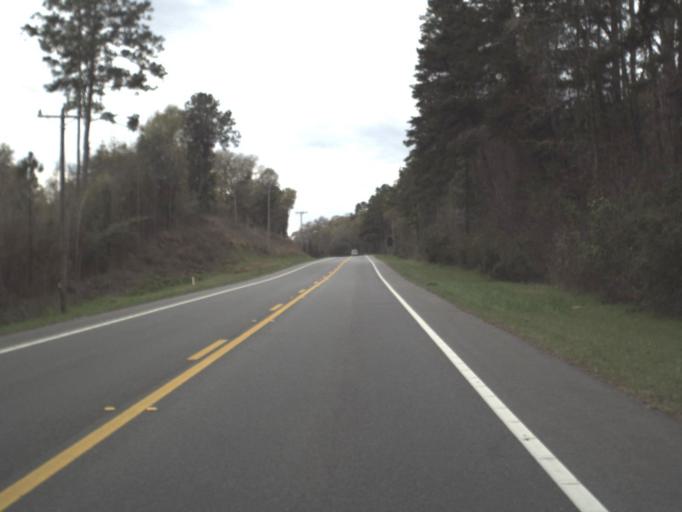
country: US
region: Florida
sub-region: Gadsden County
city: Quincy
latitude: 30.4886
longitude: -84.6188
